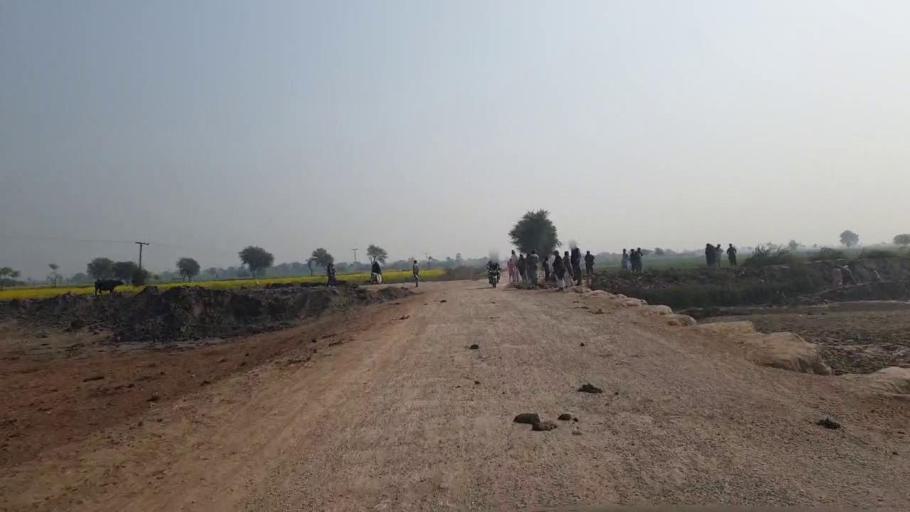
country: PK
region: Sindh
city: Hala
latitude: 25.9407
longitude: 68.4474
